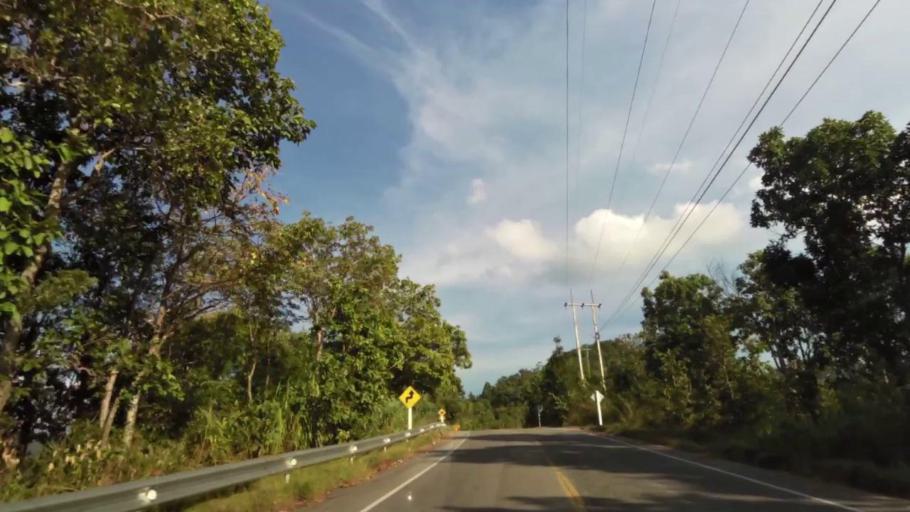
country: TH
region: Chiang Rai
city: Khun Tan
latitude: 19.8785
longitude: 100.3108
